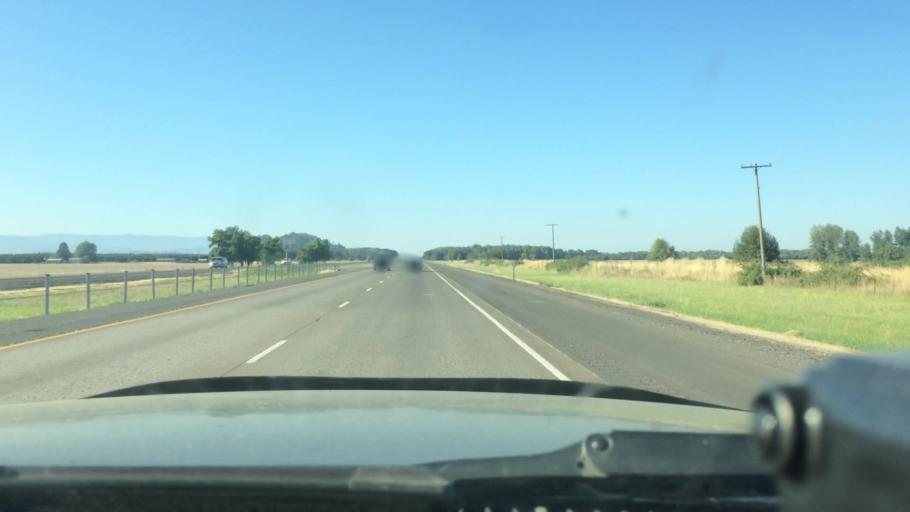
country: US
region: Oregon
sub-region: Linn County
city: Tangent
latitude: 44.4905
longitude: -123.0618
